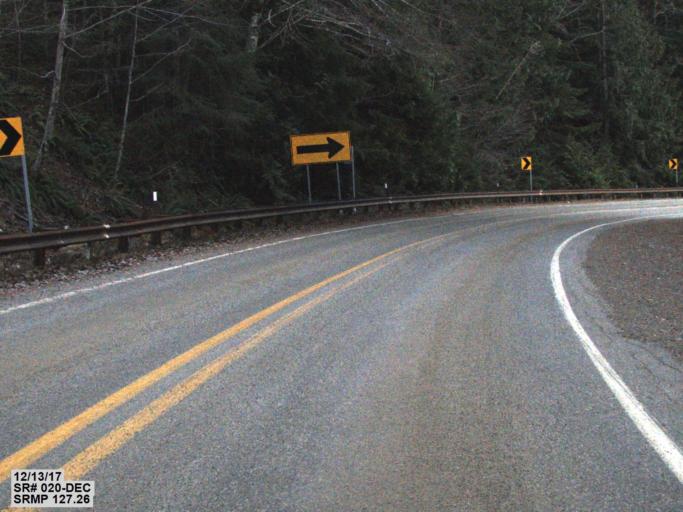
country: US
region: Washington
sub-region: Snohomish County
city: Darrington
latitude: 48.7081
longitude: -121.1378
